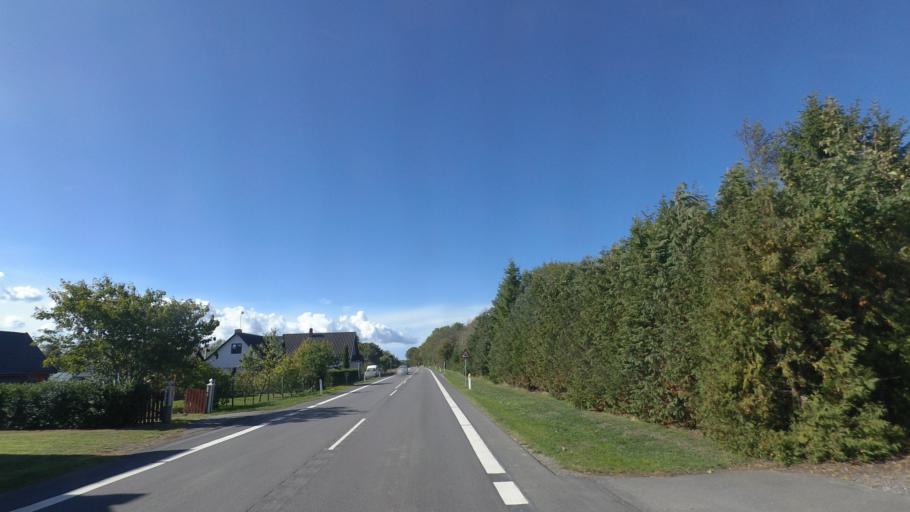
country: DK
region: Capital Region
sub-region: Bornholm Kommune
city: Akirkeby
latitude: 55.0676
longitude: 14.9976
